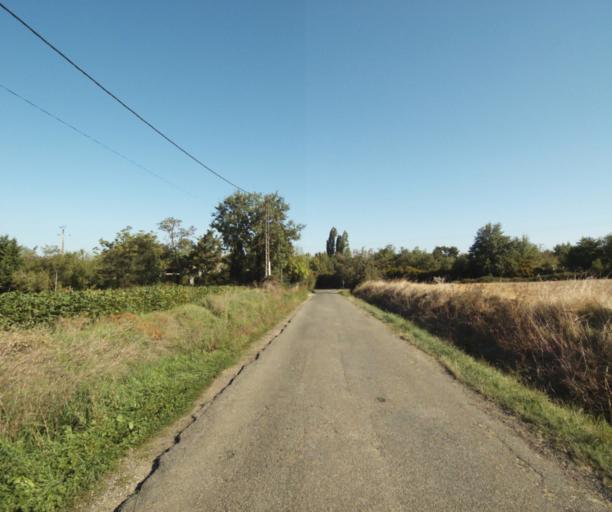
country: FR
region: Midi-Pyrenees
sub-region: Departement du Tarn-et-Garonne
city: Verdun-sur-Garonne
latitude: 43.8585
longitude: 1.2111
